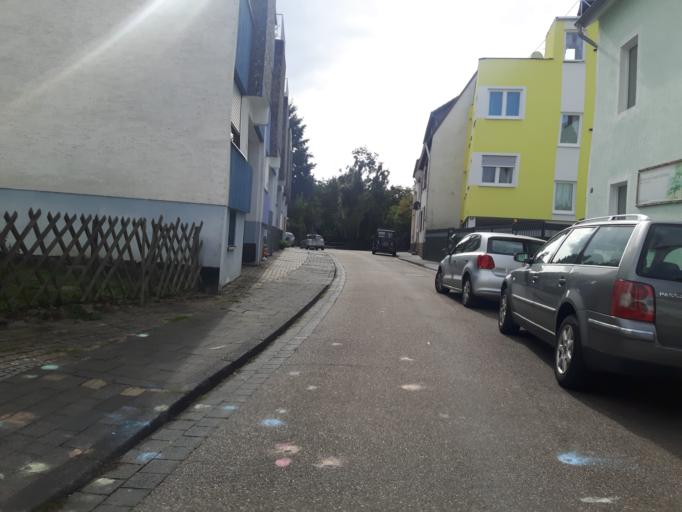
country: DE
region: Rheinland-Pfalz
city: Kaltenengers
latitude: 50.4223
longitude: 7.5559
